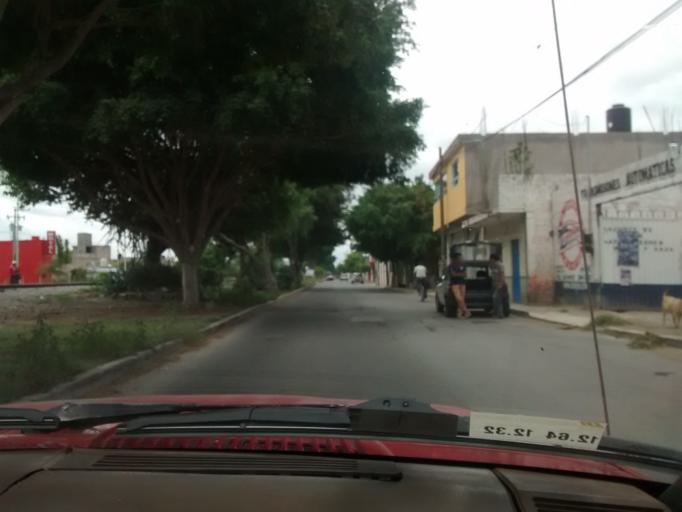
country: MX
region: Puebla
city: Tehuacan
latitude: 18.4774
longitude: -97.4098
